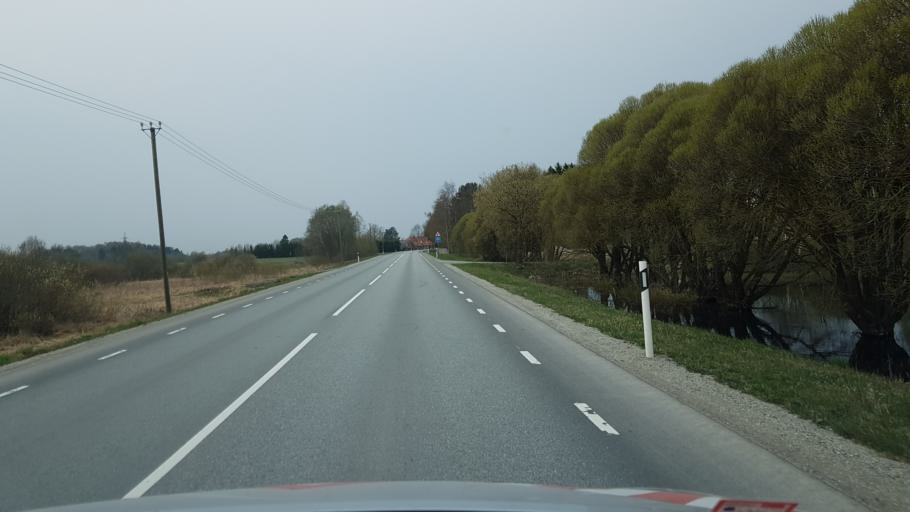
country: EE
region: Harju
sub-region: Joelaehtme vald
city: Loo
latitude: 59.3930
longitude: 24.9715
